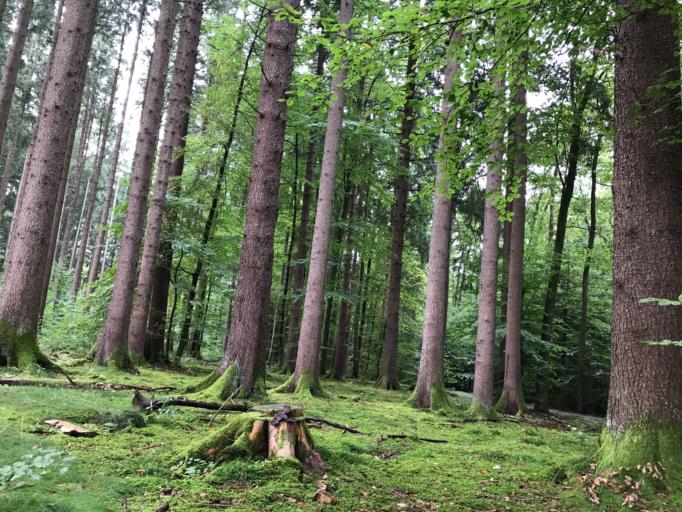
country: DE
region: Bavaria
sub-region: Upper Bavaria
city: Grunwald
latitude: 48.0237
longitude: 11.5337
